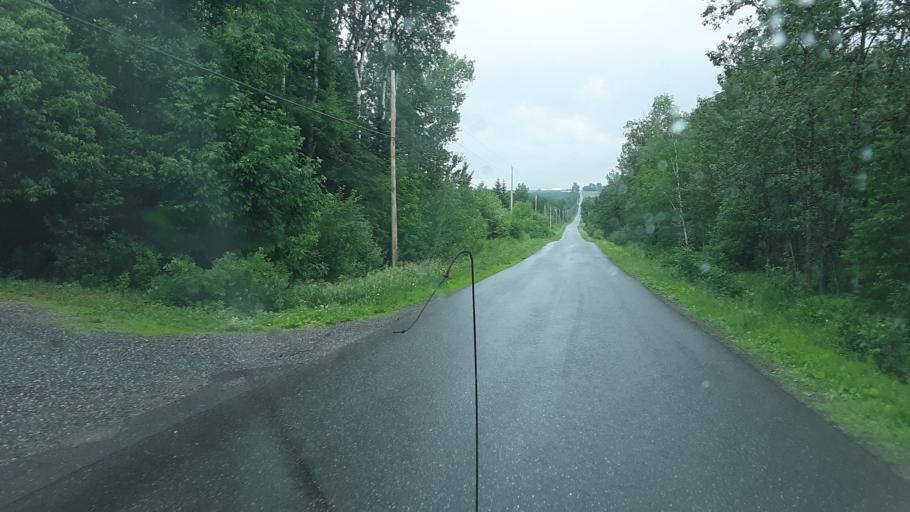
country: US
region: Maine
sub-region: Aroostook County
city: Presque Isle
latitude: 46.6812
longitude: -68.2158
